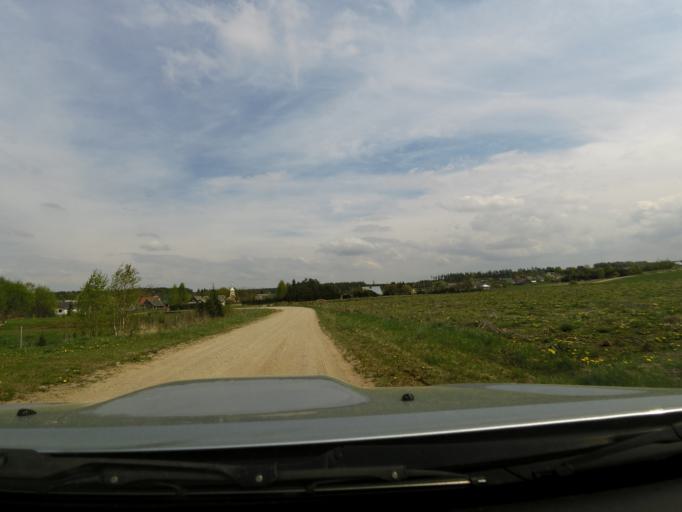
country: LT
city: Salcininkai
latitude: 54.4177
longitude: 25.3180
